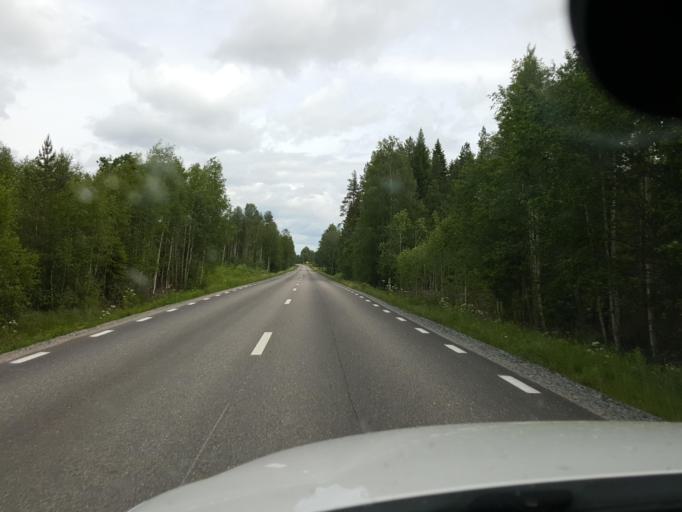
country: SE
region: Gaevleborg
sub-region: Ljusdals Kommun
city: Farila
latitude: 61.7957
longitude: 15.7065
